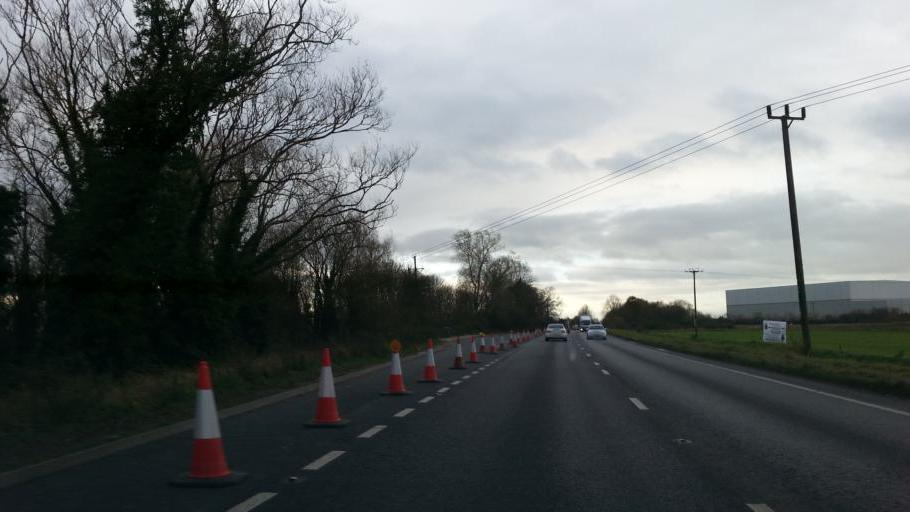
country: GB
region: England
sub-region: Cambridgeshire
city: Wisbech
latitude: 52.6464
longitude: 0.1642
